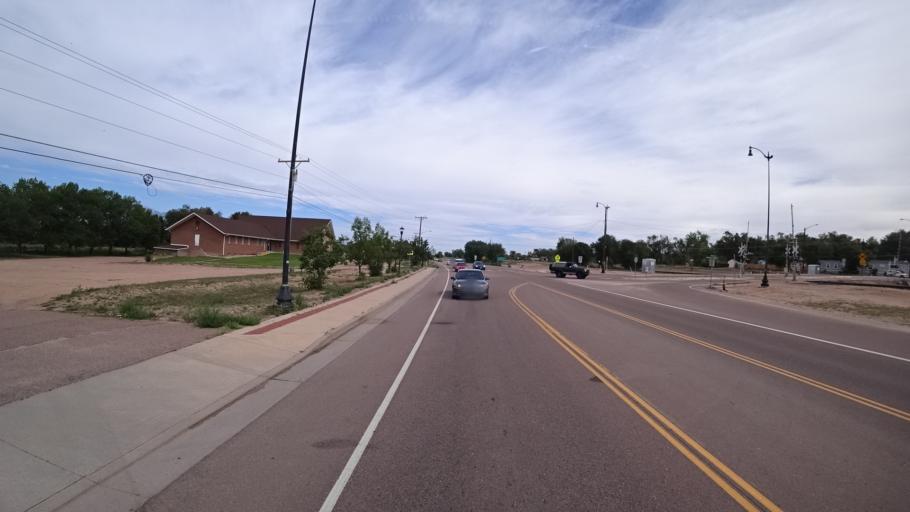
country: US
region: Colorado
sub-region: El Paso County
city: Fountain
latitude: 38.6962
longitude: -104.7054
